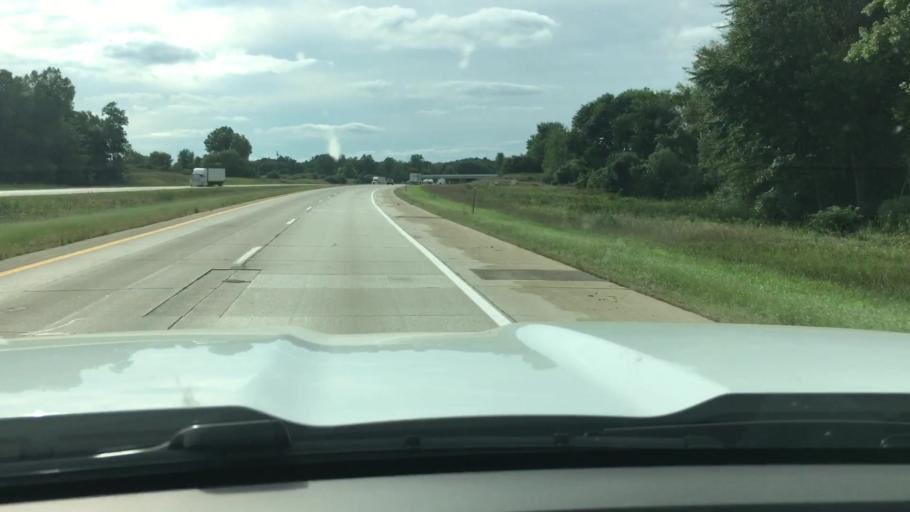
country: US
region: Michigan
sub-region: Lapeer County
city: Lapeer
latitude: 43.0120
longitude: -83.2743
